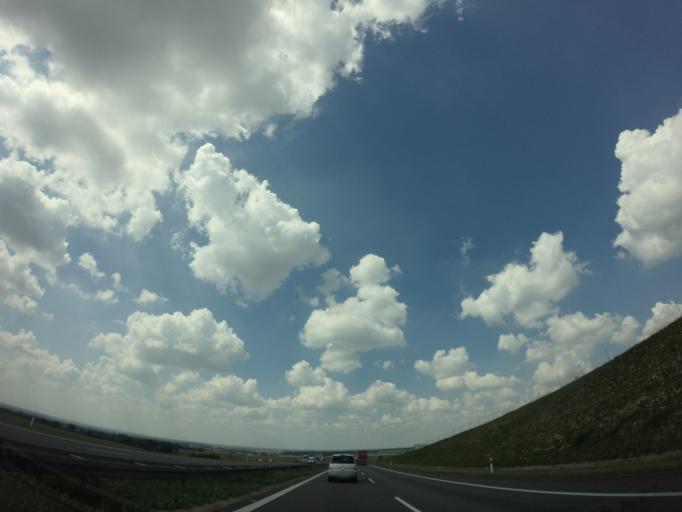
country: PL
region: Opole Voivodeship
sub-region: Powiat krapkowicki
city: Rozwadza
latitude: 50.4807
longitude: 18.1210
